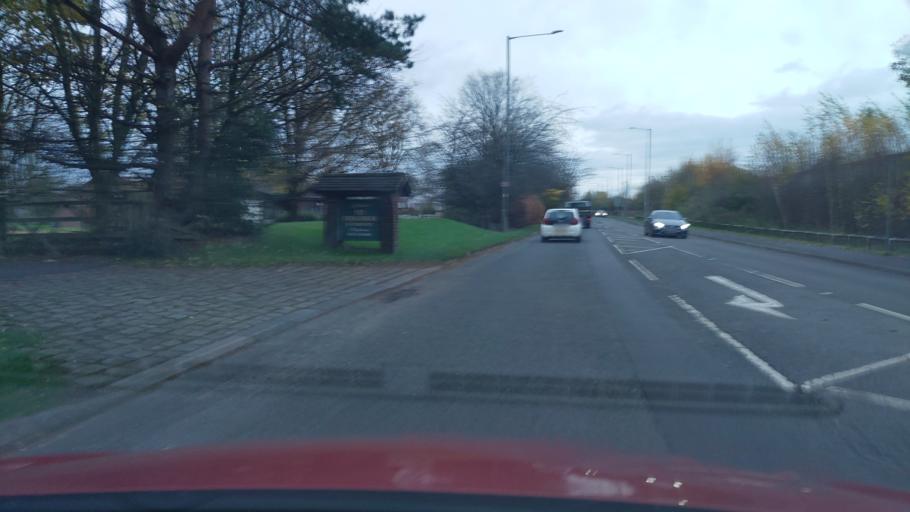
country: GB
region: England
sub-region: Lancashire
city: Euxton
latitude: 53.6818
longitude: -2.6767
